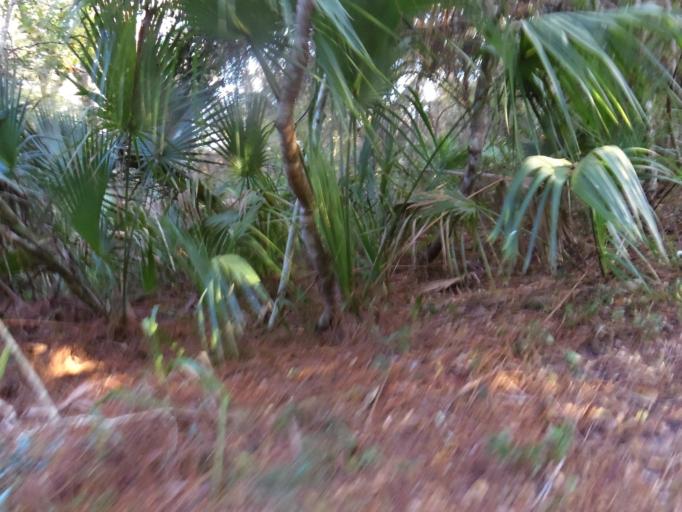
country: US
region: Florida
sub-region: Duval County
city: Atlantic Beach
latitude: 30.4750
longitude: -81.4181
